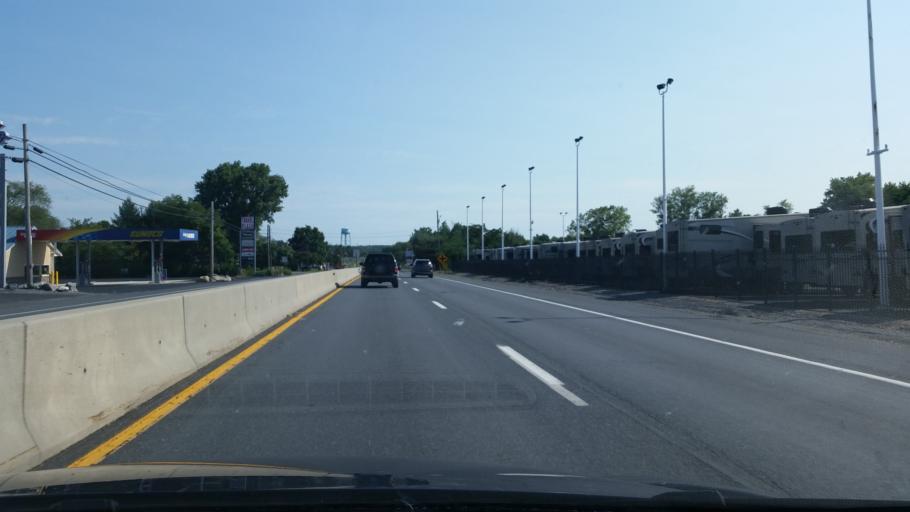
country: US
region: Pennsylvania
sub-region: Berks County
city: Shoemakersville
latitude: 40.5145
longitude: -75.9676
